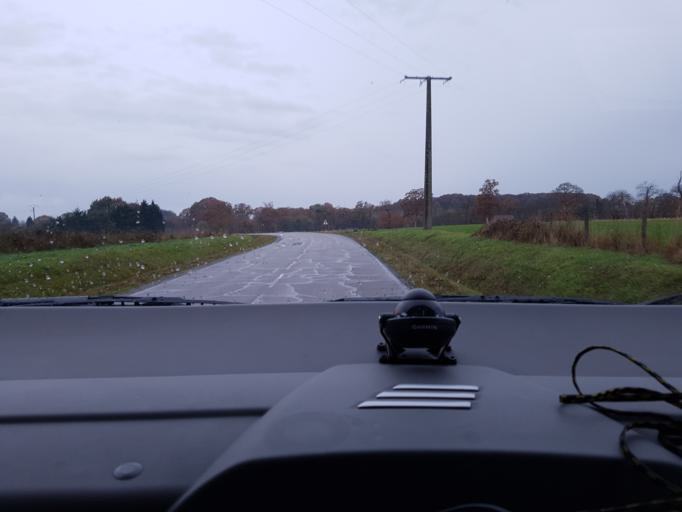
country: FR
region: Brittany
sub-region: Departement d'Ille-et-Vilaine
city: Saint-Brice-en-Cogles
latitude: 48.3990
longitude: -1.3760
